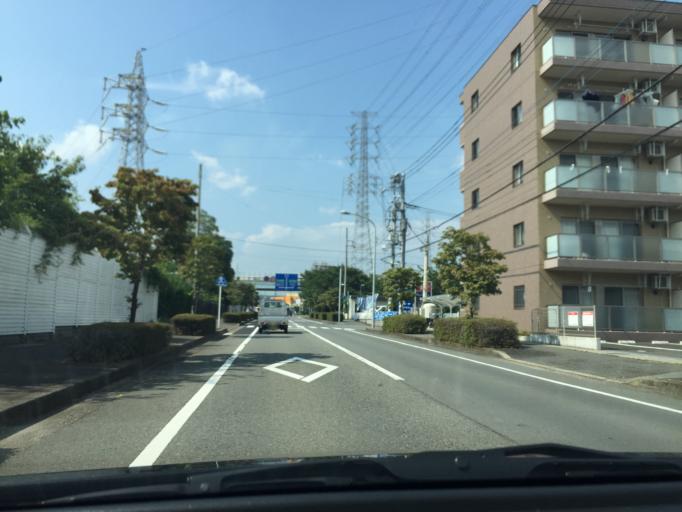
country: JP
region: Shizuoka
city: Mishima
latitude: 35.1474
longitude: 138.9050
